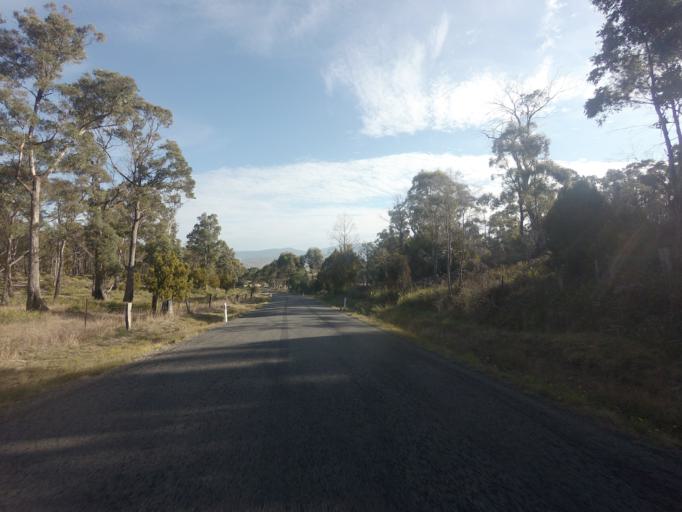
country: AU
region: Tasmania
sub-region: Brighton
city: Bridgewater
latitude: -42.5147
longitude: 147.3872
